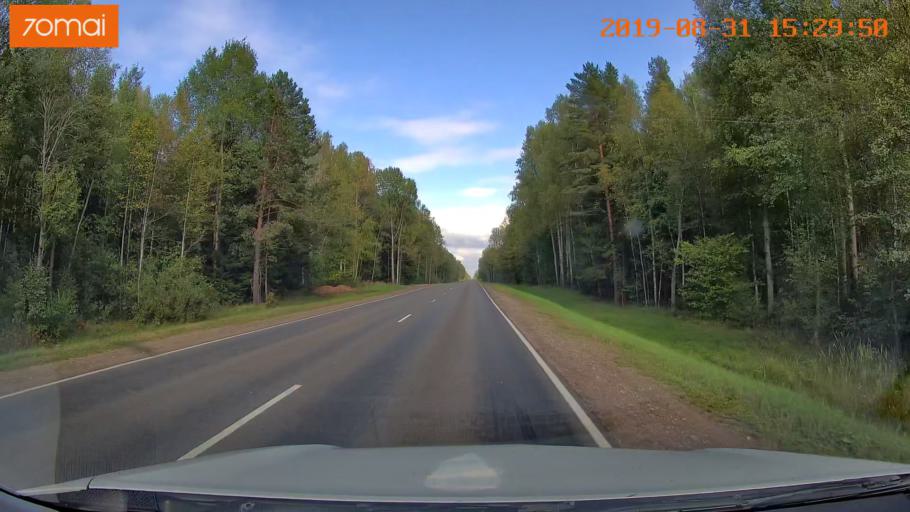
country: RU
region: Kaluga
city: Baryatino
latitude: 54.5716
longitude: 34.6154
